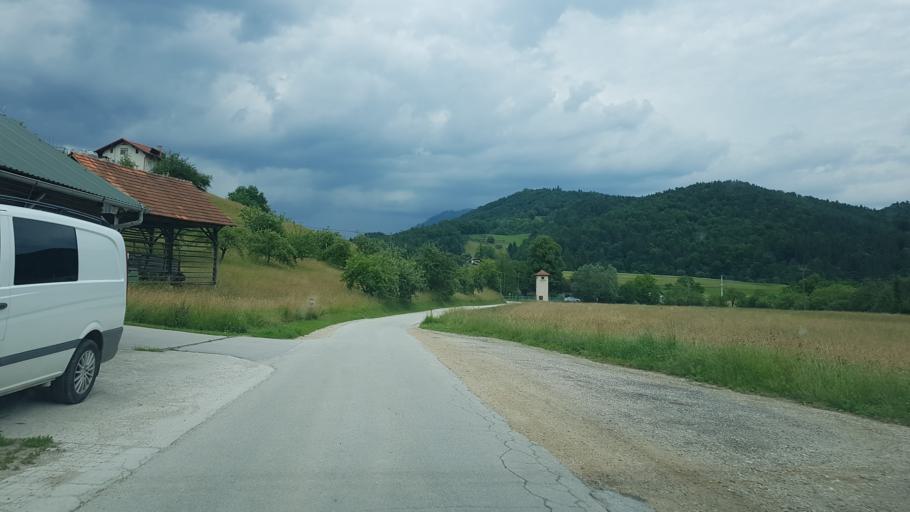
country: SI
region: Dobrna
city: Dobrna
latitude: 46.3404
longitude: 15.2701
